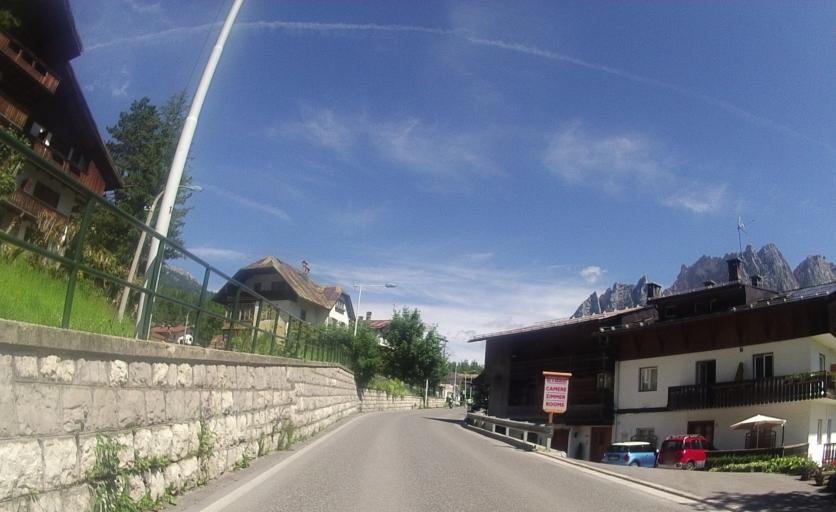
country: IT
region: Veneto
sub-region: Provincia di Belluno
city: Cortina d'Ampezzo
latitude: 46.5411
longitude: 12.1293
